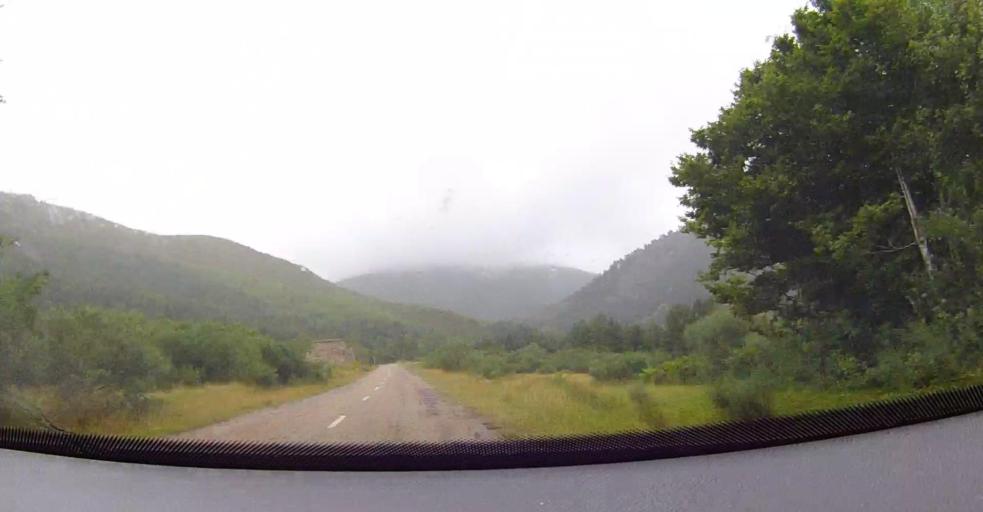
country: ES
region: Castille and Leon
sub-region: Provincia de Leon
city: Puebla de Lillo
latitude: 43.0653
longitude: -5.2696
